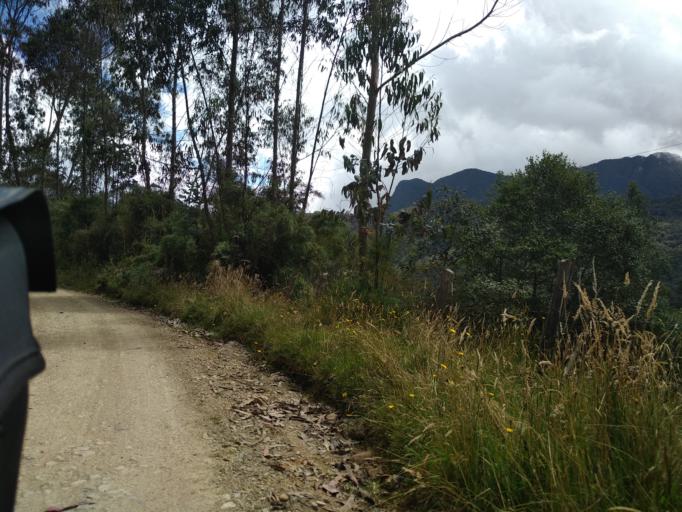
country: CO
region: Boyaca
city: Duitama
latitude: 5.9437
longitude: -73.1304
